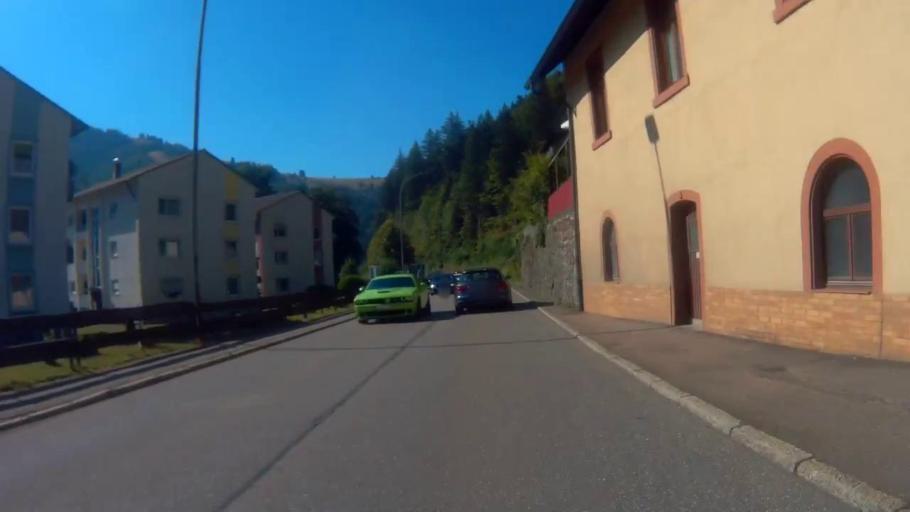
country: DE
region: Baden-Wuerttemberg
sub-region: Freiburg Region
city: Schonau im Schwarzwald
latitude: 47.7837
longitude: 7.8926
